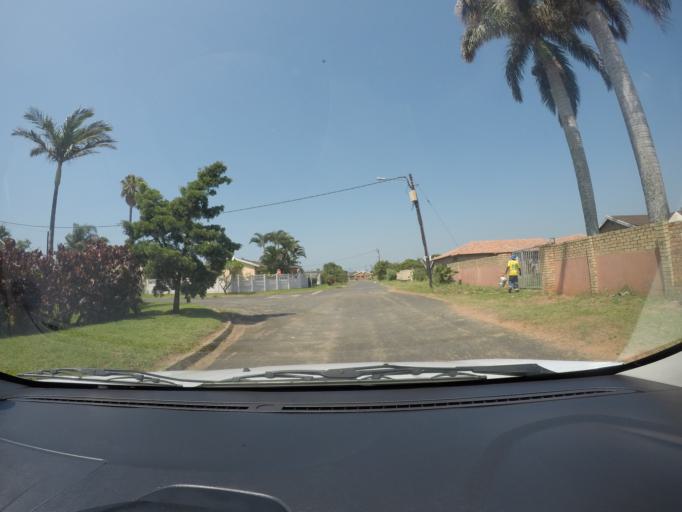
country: ZA
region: KwaZulu-Natal
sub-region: uThungulu District Municipality
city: eSikhawini
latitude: -28.8614
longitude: 31.9228
